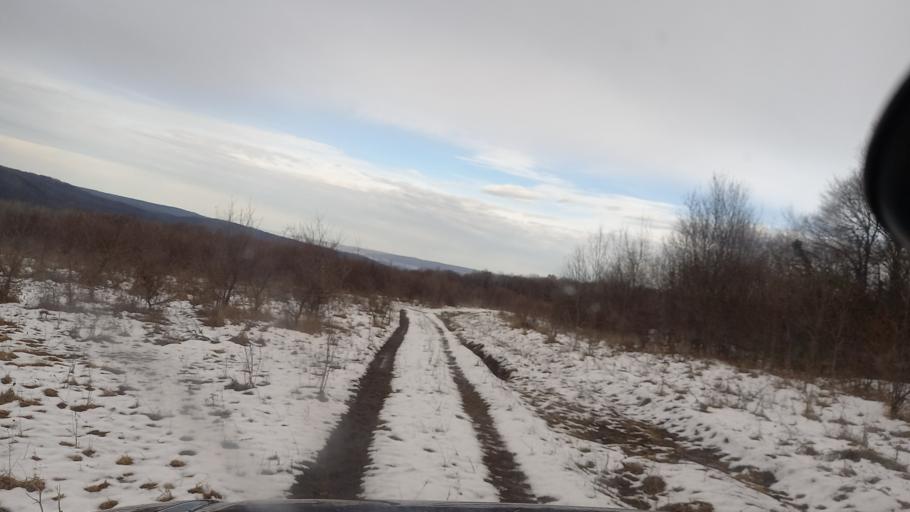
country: RU
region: Adygeya
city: Kamennomostskiy
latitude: 44.2516
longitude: 40.1791
